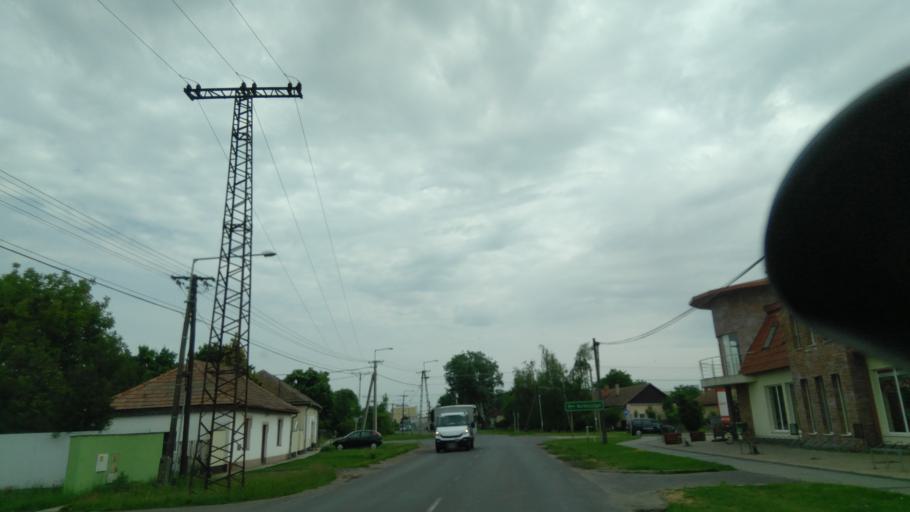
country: HU
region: Bekes
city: Szeghalom
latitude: 47.0286
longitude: 21.1684
